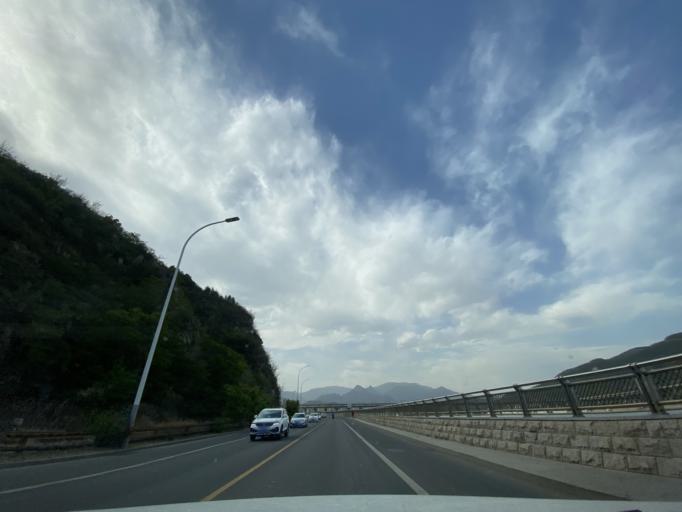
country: CN
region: Beijing
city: Chengzi
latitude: 39.9597
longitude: 116.0920
